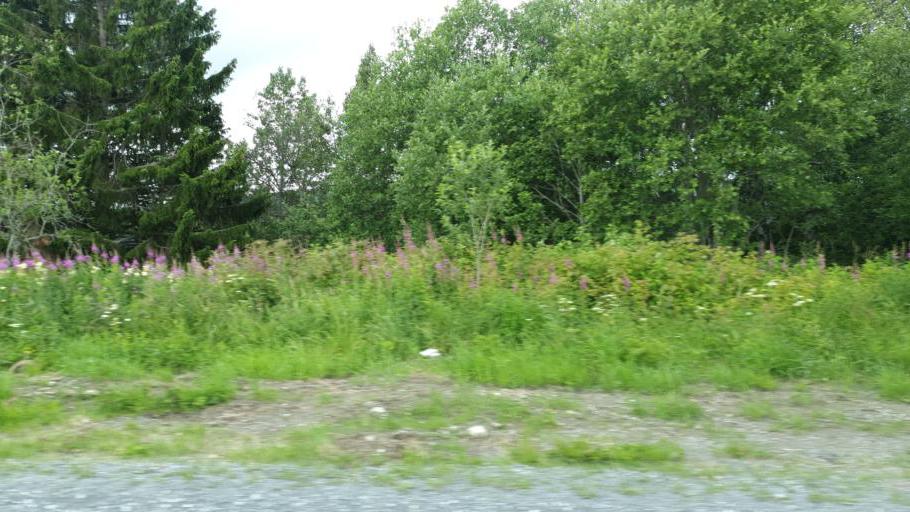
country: NO
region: Sor-Trondelag
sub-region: Rennebu
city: Berkak
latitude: 62.8218
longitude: 10.0154
